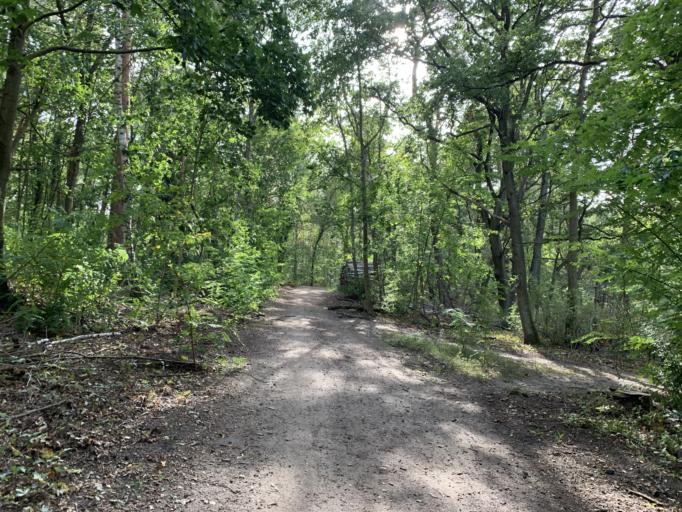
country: DE
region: Berlin
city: Wannsee
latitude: 52.4105
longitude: 13.1543
